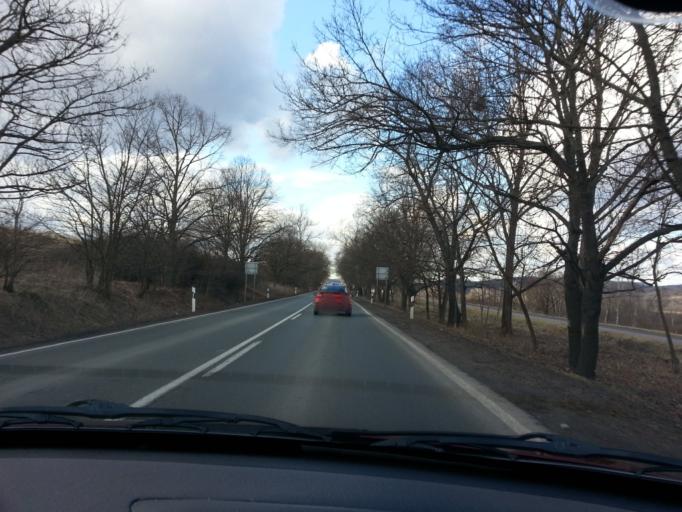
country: HU
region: Nograd
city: Kazar
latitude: 48.0253
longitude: 19.8170
